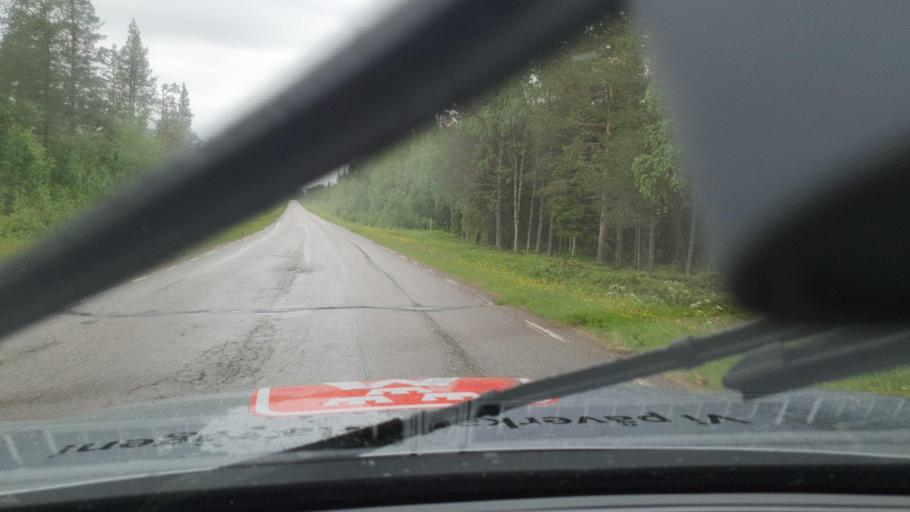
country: SE
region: Norrbotten
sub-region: Pajala Kommun
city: Pajala
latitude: 66.8195
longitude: 23.1160
